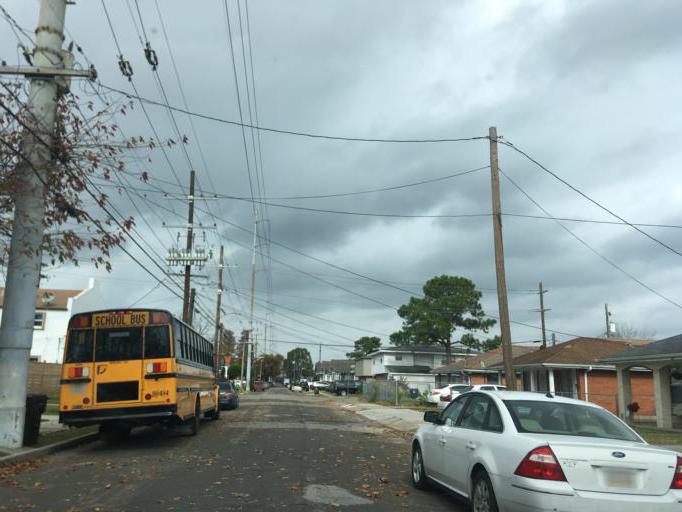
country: US
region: Louisiana
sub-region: Orleans Parish
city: New Orleans
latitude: 29.9943
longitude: -90.0602
